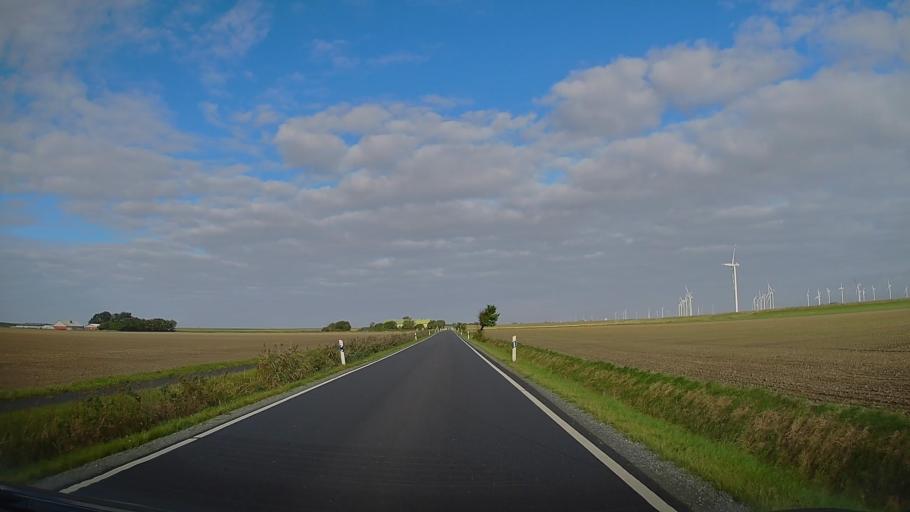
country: DE
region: Schleswig-Holstein
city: Reussenkoge
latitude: 54.5869
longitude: 8.9215
